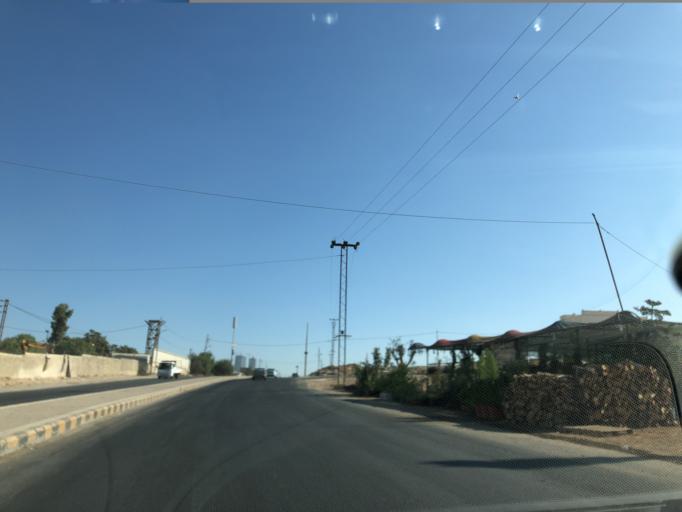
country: JO
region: Amman
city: Wadi as Sir
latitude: 31.9351
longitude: 35.8478
